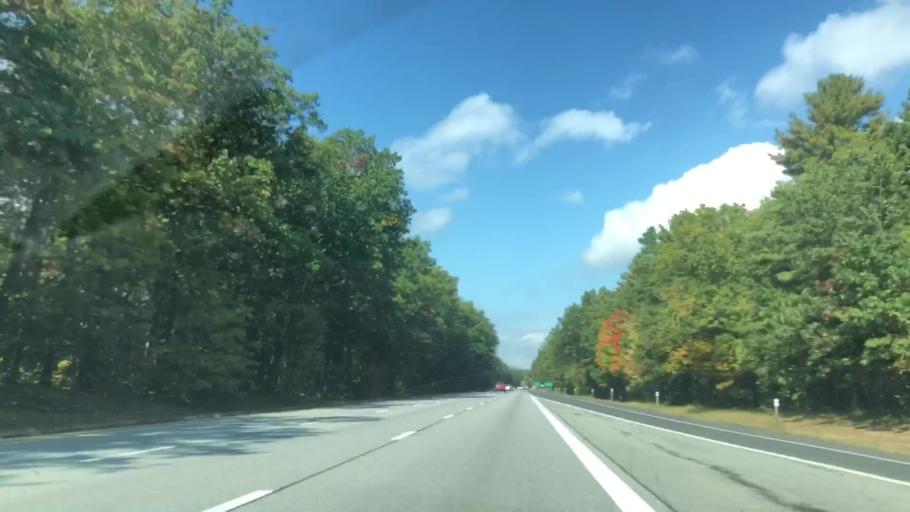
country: US
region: New York
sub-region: Warren County
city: West Glens Falls
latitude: 43.2749
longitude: -73.6759
